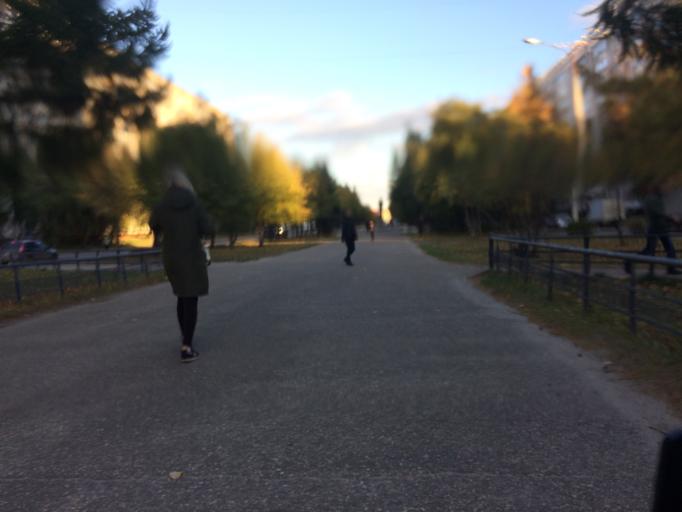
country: RU
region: Mariy-El
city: Yoshkar-Ola
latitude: 56.6318
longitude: 47.9124
